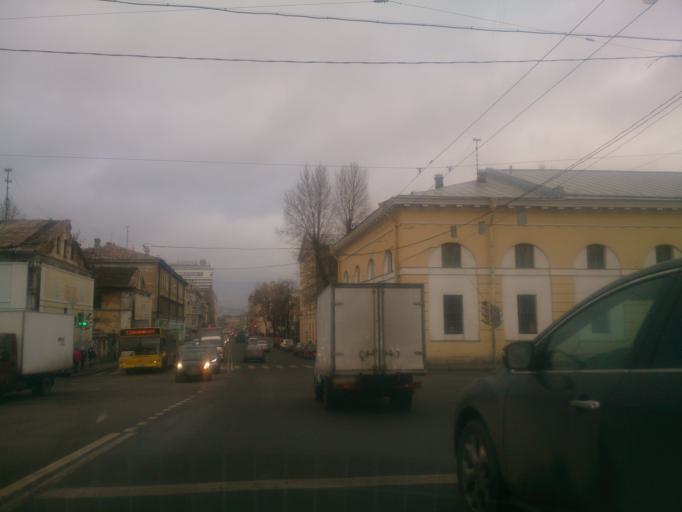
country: RU
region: St.-Petersburg
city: Admiralteisky
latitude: 59.9090
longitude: 30.2978
